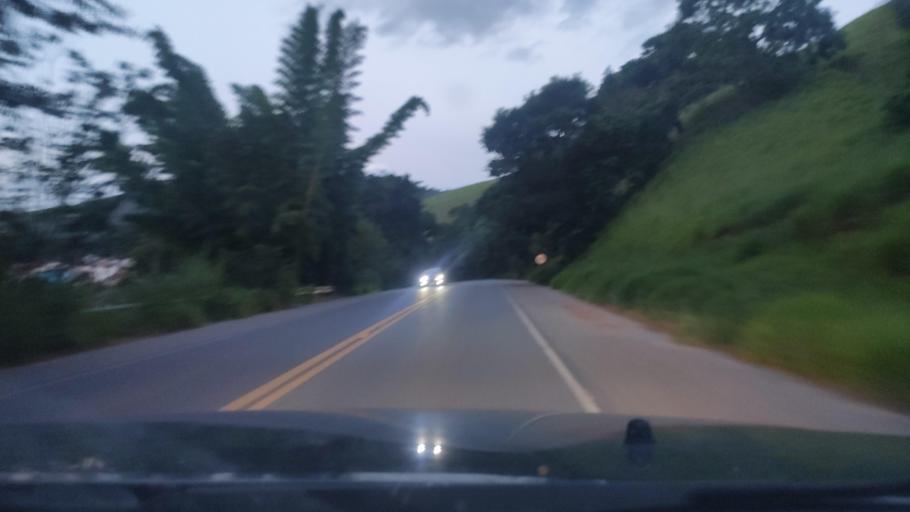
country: BR
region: Sao Paulo
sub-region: Campos Do Jordao
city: Campos do Jordao
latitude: -22.7513
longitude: -45.7427
